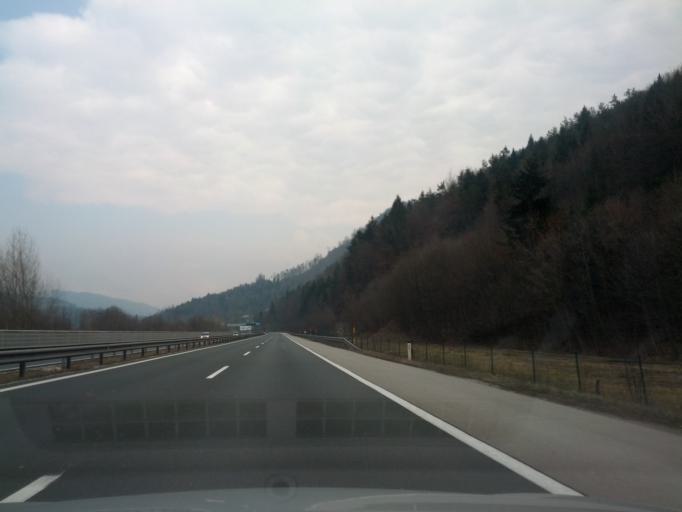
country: SI
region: Moravce
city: Moravce
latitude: 46.1641
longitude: 14.7570
